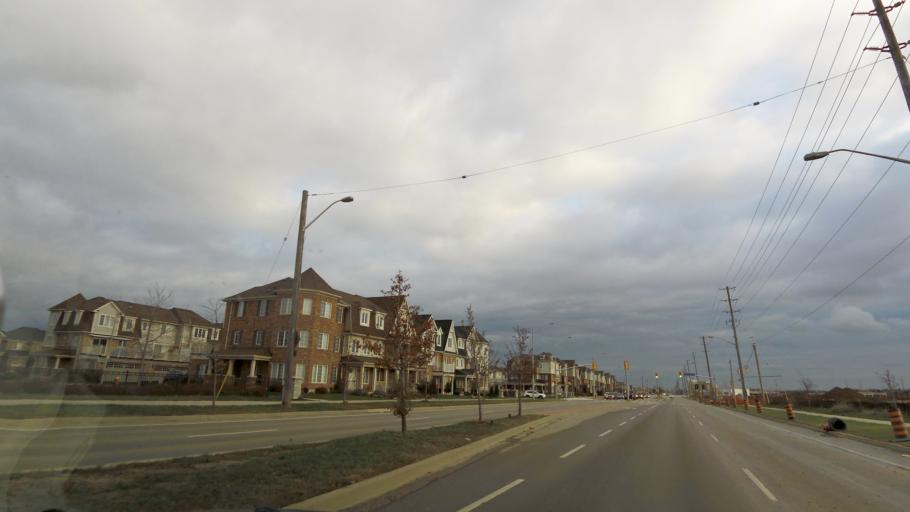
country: CA
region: Ontario
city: Burlington
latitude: 43.3953
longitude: -79.8281
